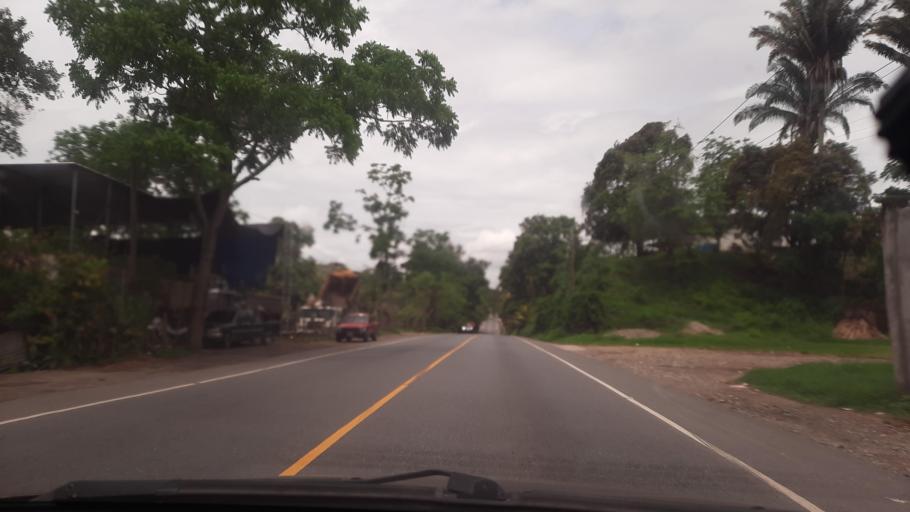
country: GT
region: Izabal
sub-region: Municipio de Los Amates
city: Los Amates
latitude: 15.2385
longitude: -89.1826
